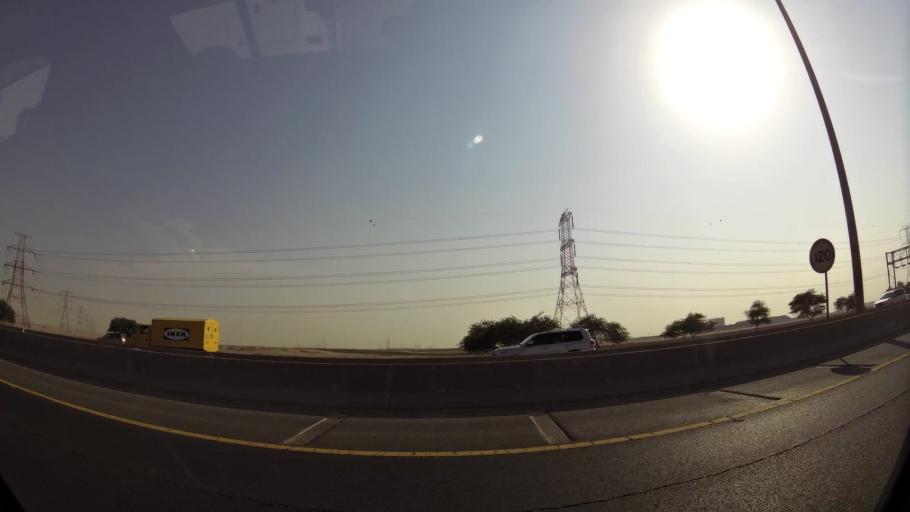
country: KW
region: Al Ahmadi
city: Al Ahmadi
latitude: 29.0228
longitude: 48.0918
